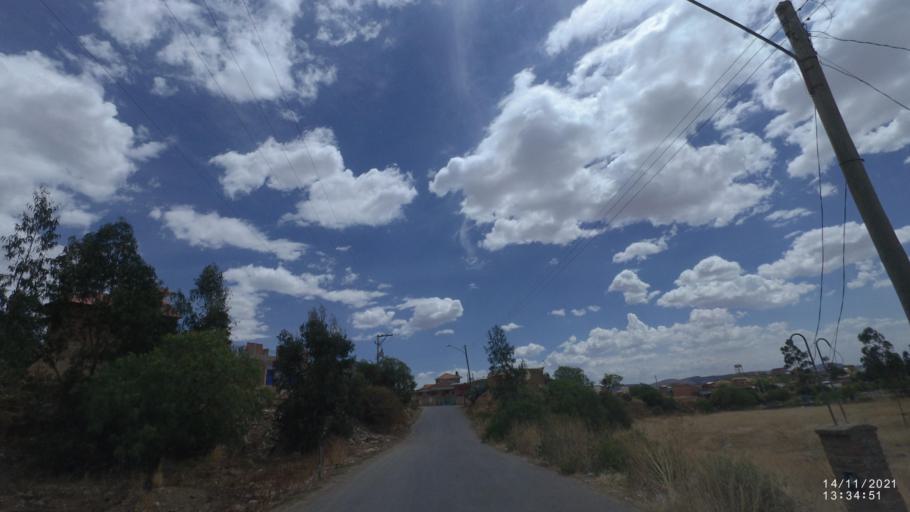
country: BO
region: Cochabamba
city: Colomi
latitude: -17.4049
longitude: -65.9859
